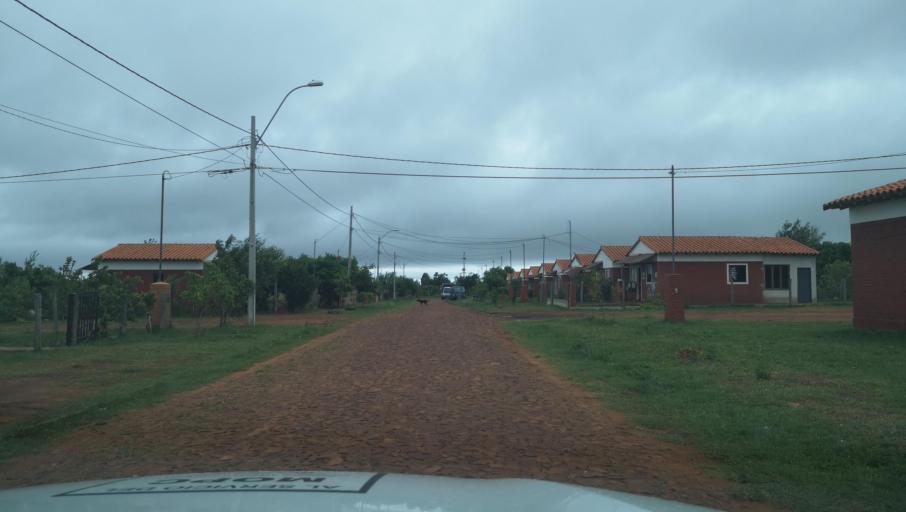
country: PY
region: Misiones
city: Santa Maria
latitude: -26.9022
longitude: -57.0378
